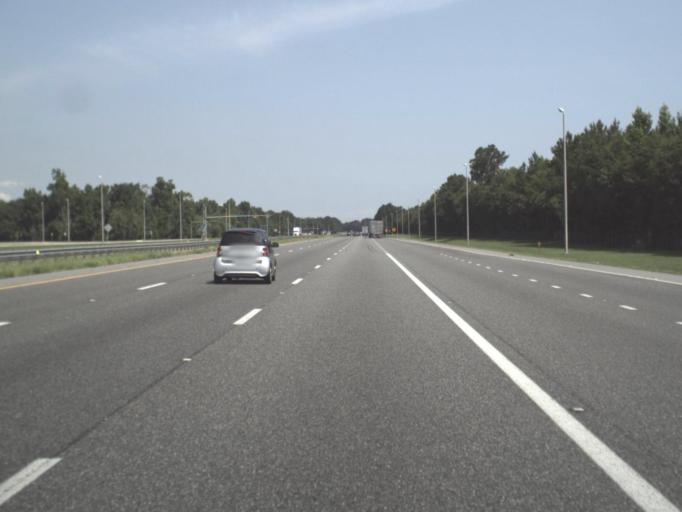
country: US
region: Florida
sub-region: Hamilton County
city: Jasper
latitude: 30.4216
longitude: -82.9020
